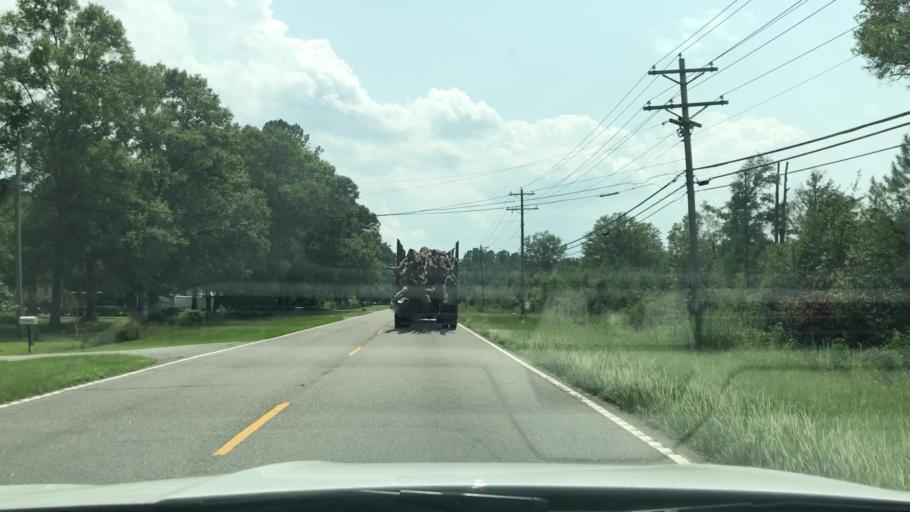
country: US
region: South Carolina
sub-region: Georgetown County
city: Georgetown
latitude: 33.4275
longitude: -79.2799
